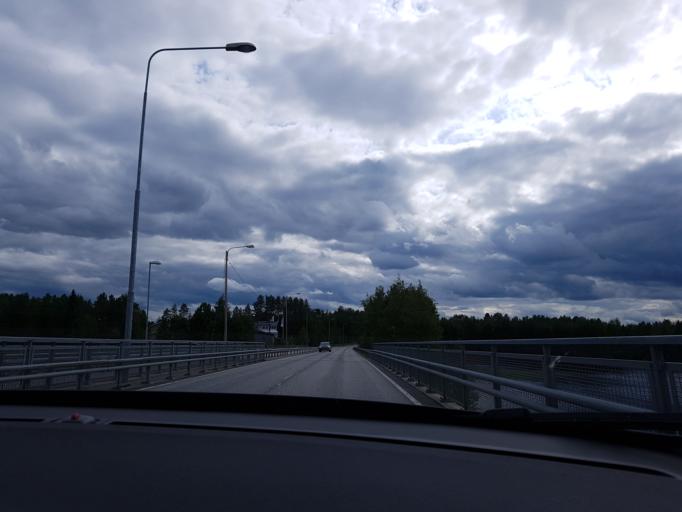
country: FI
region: Kainuu
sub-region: Kehys-Kainuu
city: Kuhmo
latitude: 64.1232
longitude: 29.5822
